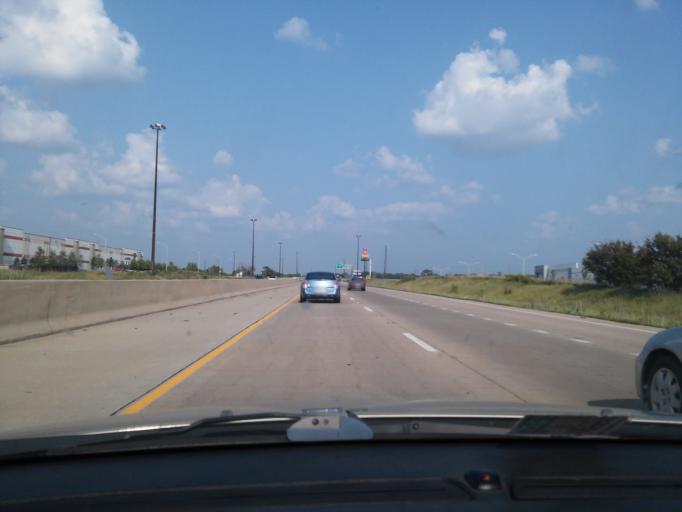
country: US
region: Illinois
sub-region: Grundy County
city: Minooka
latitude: 41.4620
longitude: -88.2812
